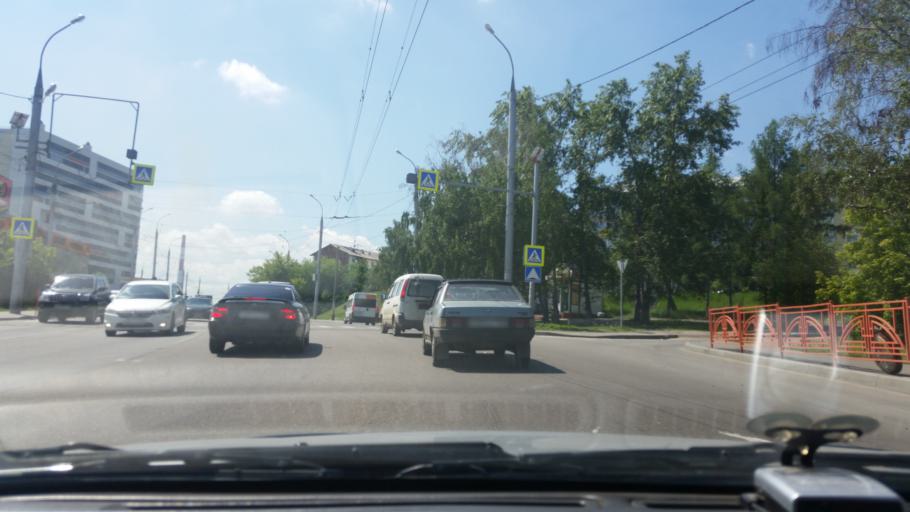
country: RU
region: Irkutsk
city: Smolenshchina
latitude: 52.2630
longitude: 104.2038
